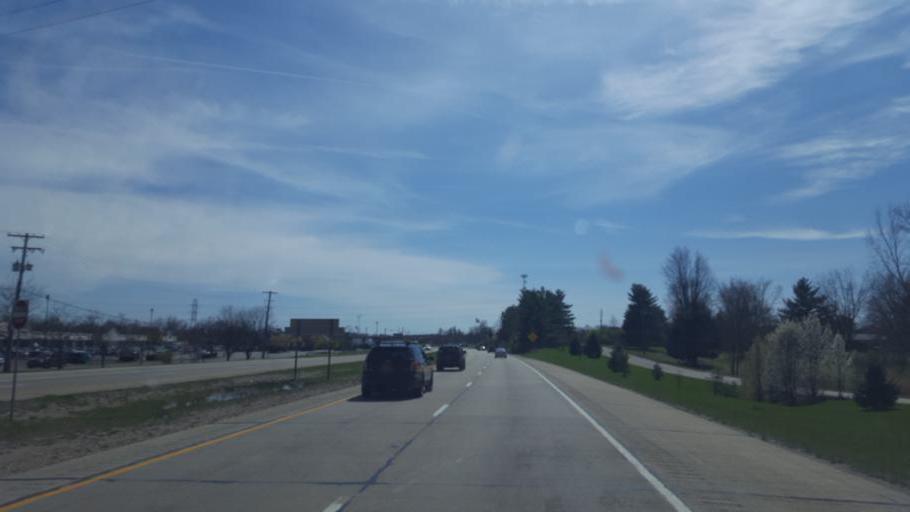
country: US
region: Ohio
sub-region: Delaware County
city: Delaware
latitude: 40.2758
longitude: -83.0706
